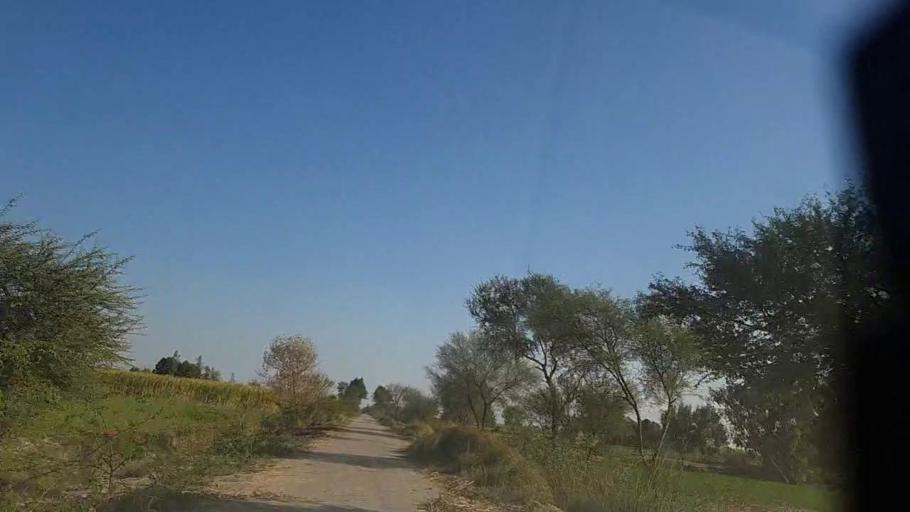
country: PK
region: Sindh
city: Digri
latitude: 25.1498
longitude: 69.0416
